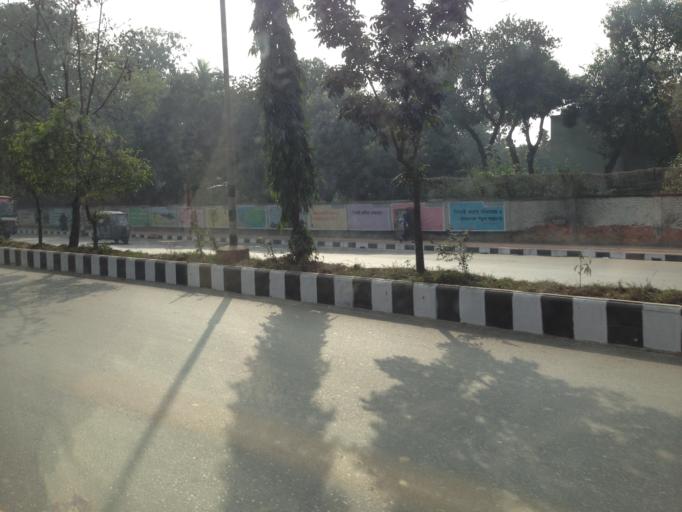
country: BD
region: Dhaka
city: Azimpur
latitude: 23.7673
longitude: 90.3694
